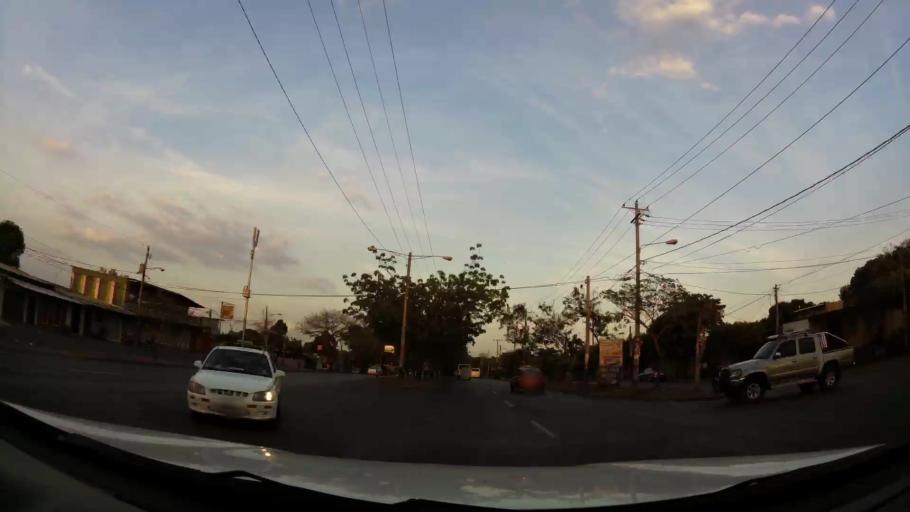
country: NI
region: Managua
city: Managua
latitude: 12.1400
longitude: -86.2130
